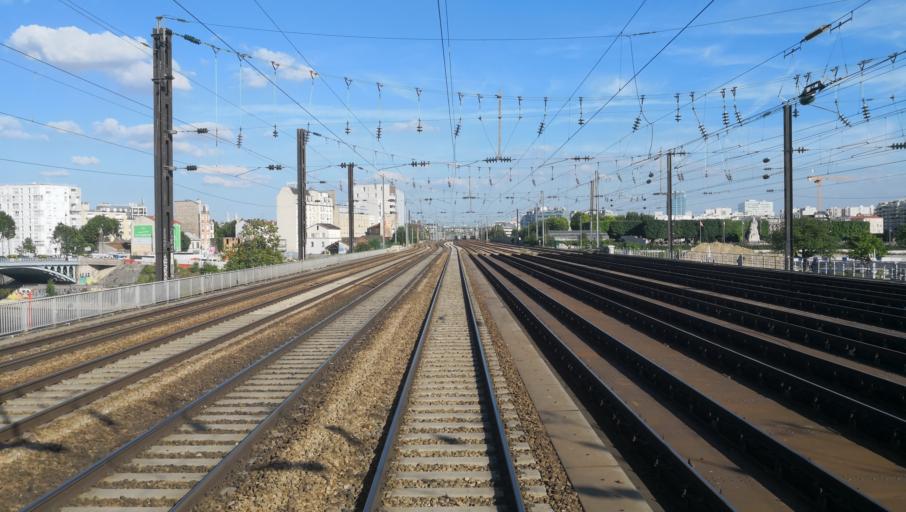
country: FR
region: Ile-de-France
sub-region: Departement des Hauts-de-Seine
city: Levallois-Perret
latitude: 48.9039
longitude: 2.2869
